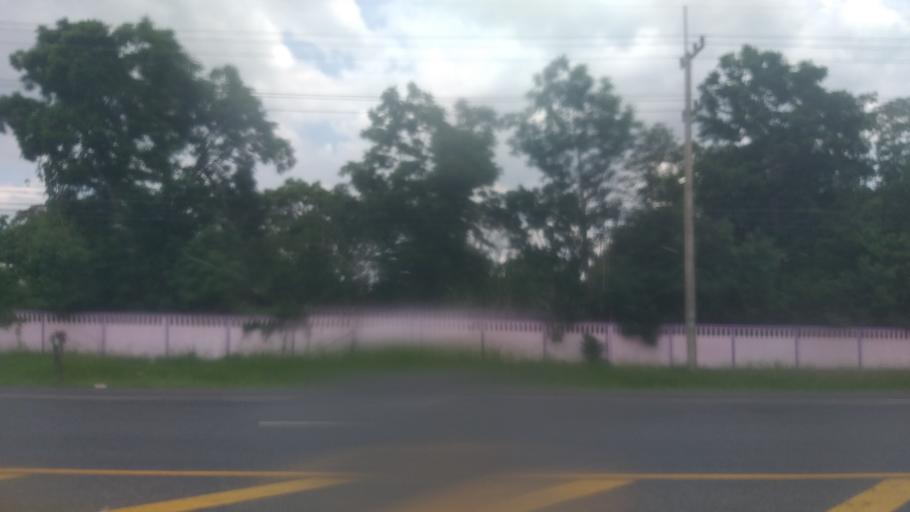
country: TH
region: Chaiyaphum
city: Noen Sa-nga
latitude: 15.6657
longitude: 101.9567
